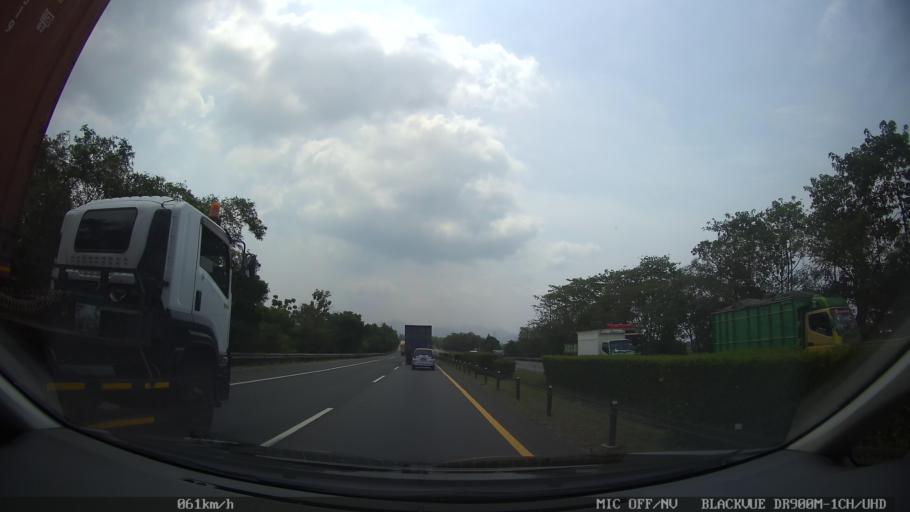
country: ID
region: Banten
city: Bojonegara
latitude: -6.0279
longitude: 106.0973
